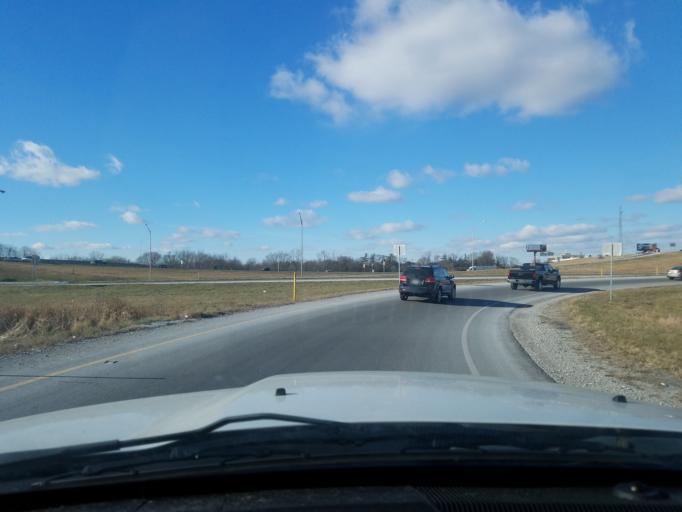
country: US
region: Indiana
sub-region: Marion County
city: Lawrence
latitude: 39.8933
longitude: -86.0544
